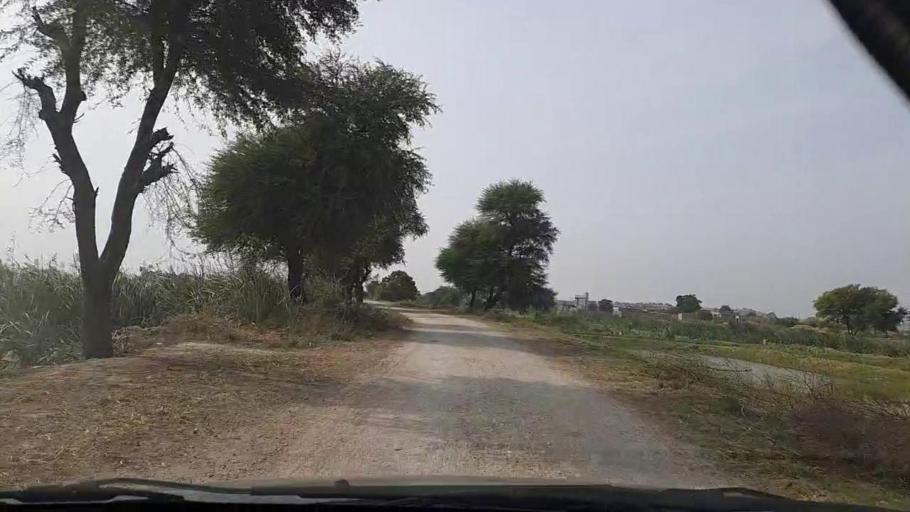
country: PK
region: Sindh
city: Thatta
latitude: 24.5782
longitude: 67.8845
